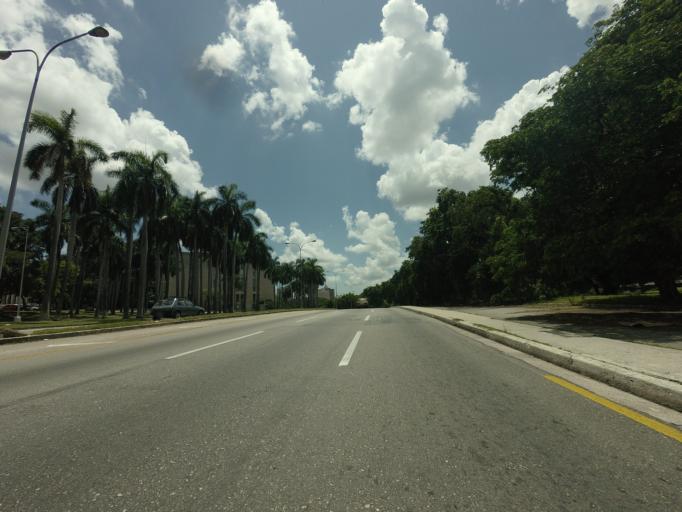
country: CU
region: La Habana
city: Havana
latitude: 23.1227
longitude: -82.3885
